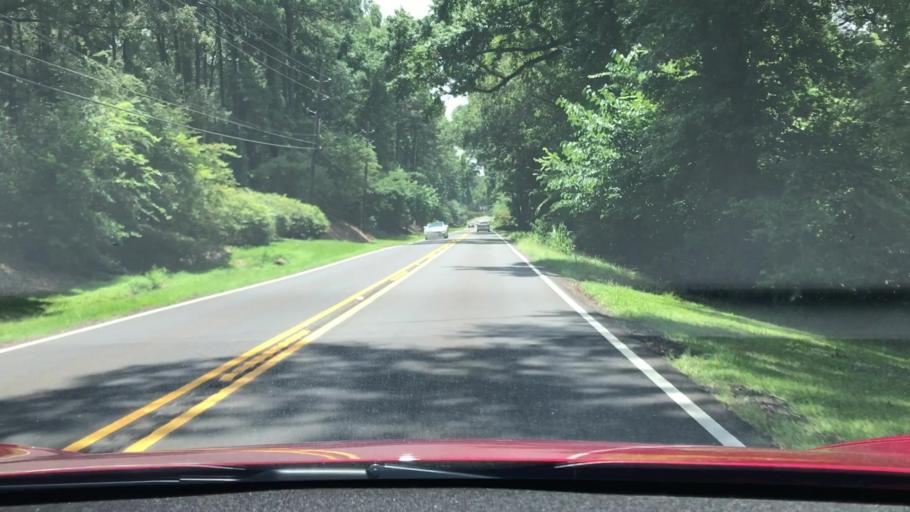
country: US
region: Louisiana
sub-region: Bossier Parish
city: Bossier City
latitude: 32.3682
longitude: -93.6849
